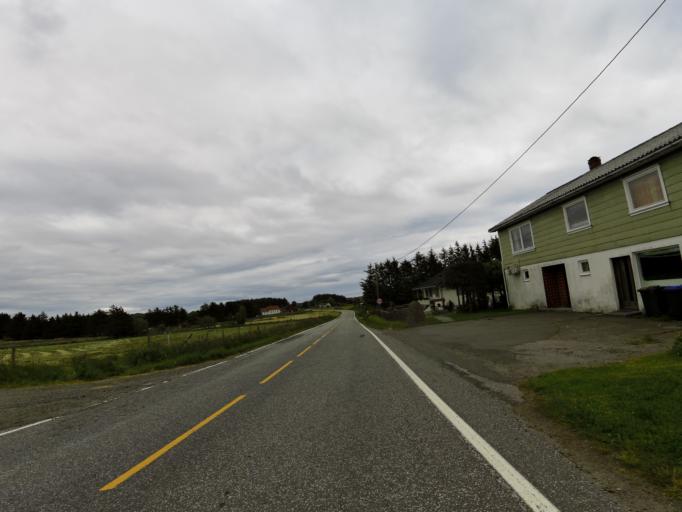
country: NO
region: Vest-Agder
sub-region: Farsund
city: Vestbygd
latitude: 58.1189
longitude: 6.6006
